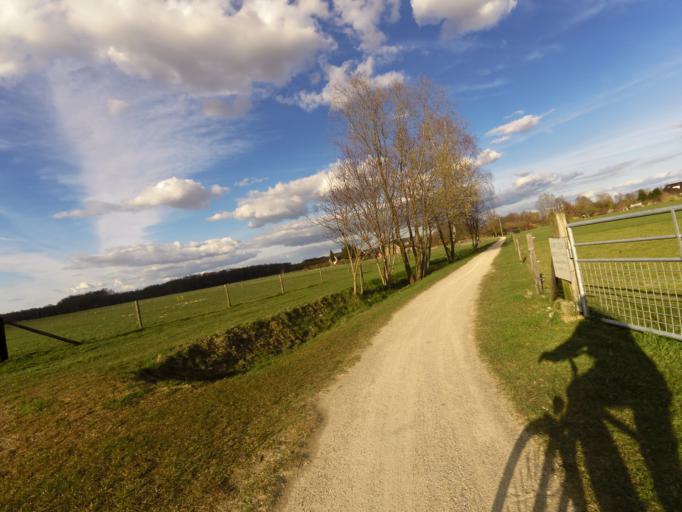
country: NL
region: Gelderland
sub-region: Gemeente Zevenaar
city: Zevenaar
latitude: 51.9397
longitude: 6.1021
